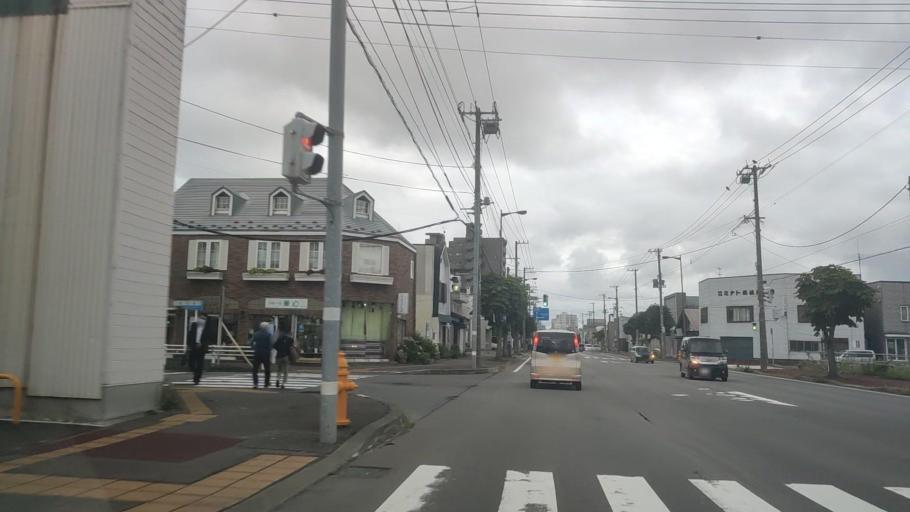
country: JP
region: Hokkaido
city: Hakodate
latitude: 41.7852
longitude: 140.7304
